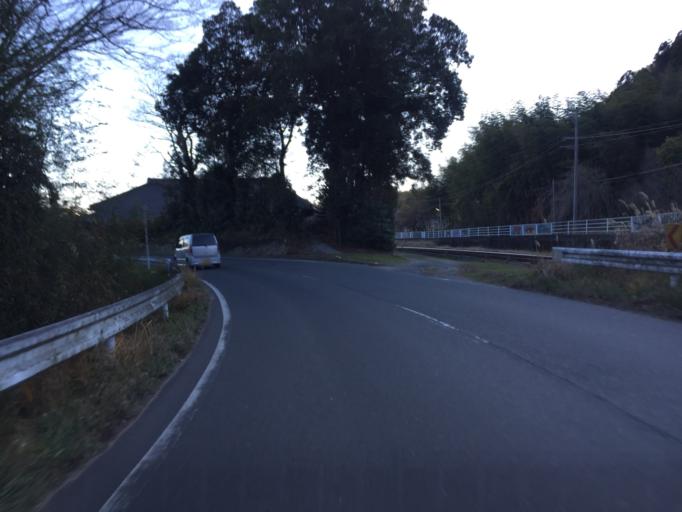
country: JP
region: Fukushima
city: Iwaki
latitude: 37.1158
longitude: 140.8596
